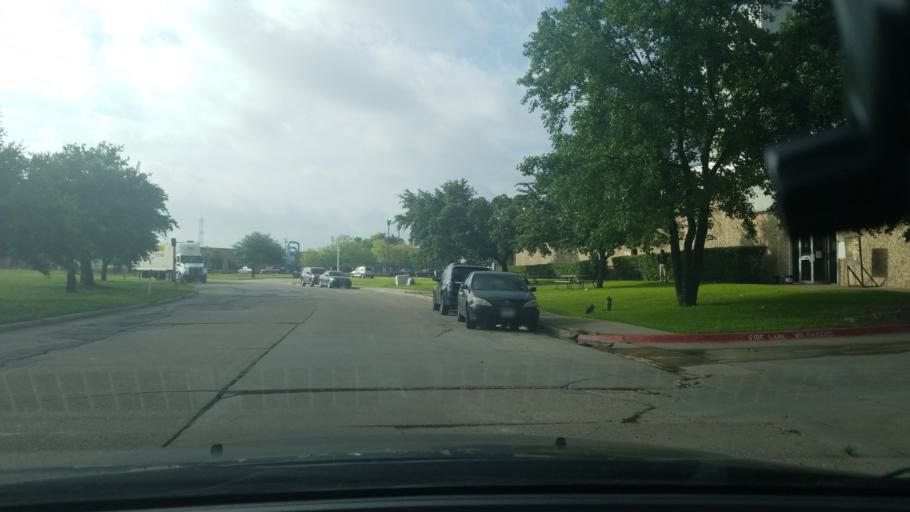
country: US
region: Texas
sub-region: Dallas County
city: Balch Springs
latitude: 32.7717
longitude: -96.6504
